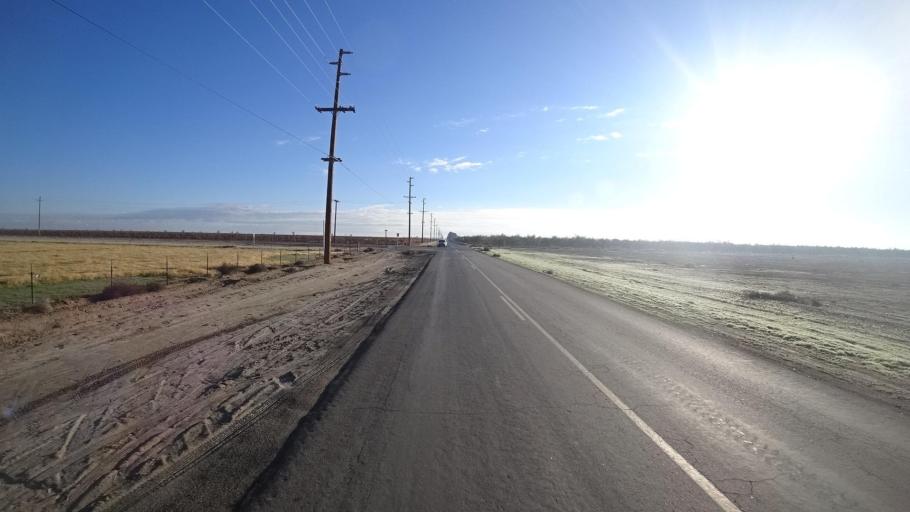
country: US
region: California
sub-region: Kern County
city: Delano
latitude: 35.7903
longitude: -119.2868
